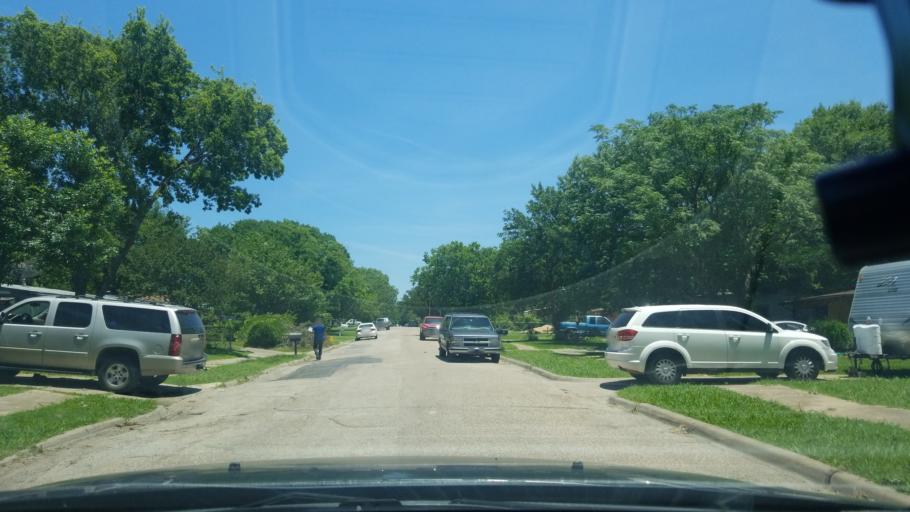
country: US
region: Texas
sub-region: Dallas County
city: Mesquite
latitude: 32.7798
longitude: -96.6049
